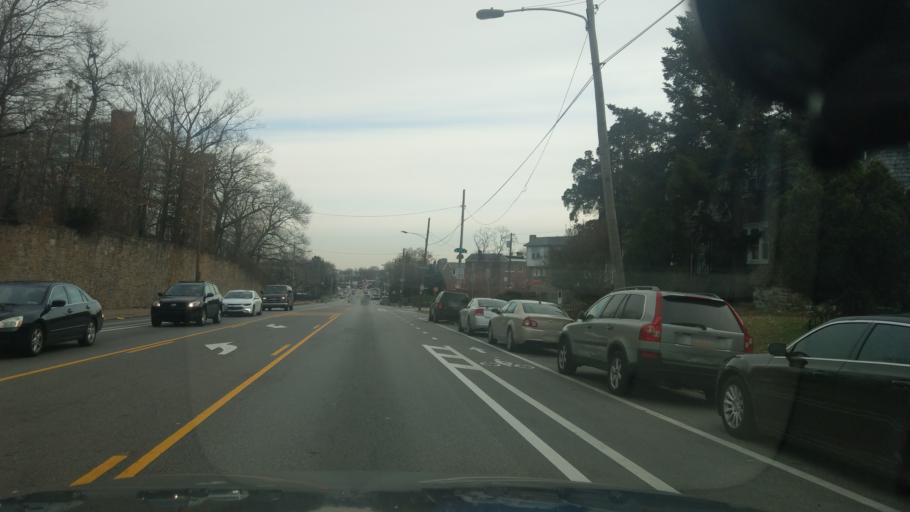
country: US
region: Pennsylvania
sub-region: Montgomery County
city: Wyncote
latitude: 40.0502
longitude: -75.1478
